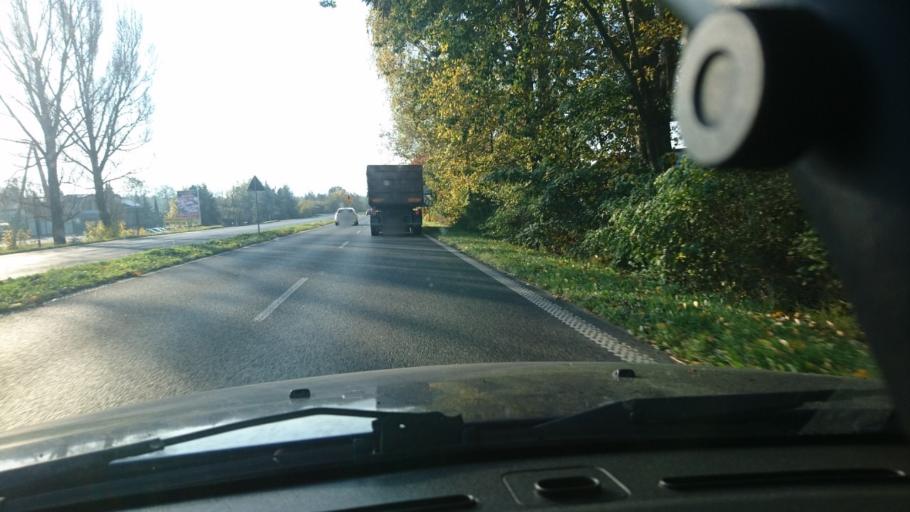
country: PL
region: Silesian Voivodeship
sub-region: Powiat cieszynski
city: Gorki Wielkie
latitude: 49.7807
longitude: 18.8071
